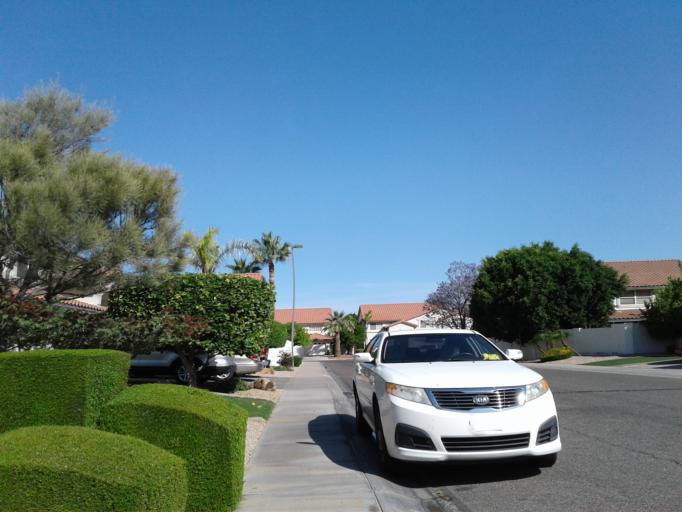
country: US
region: Arizona
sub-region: Maricopa County
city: Peoria
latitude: 33.6004
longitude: -112.1806
